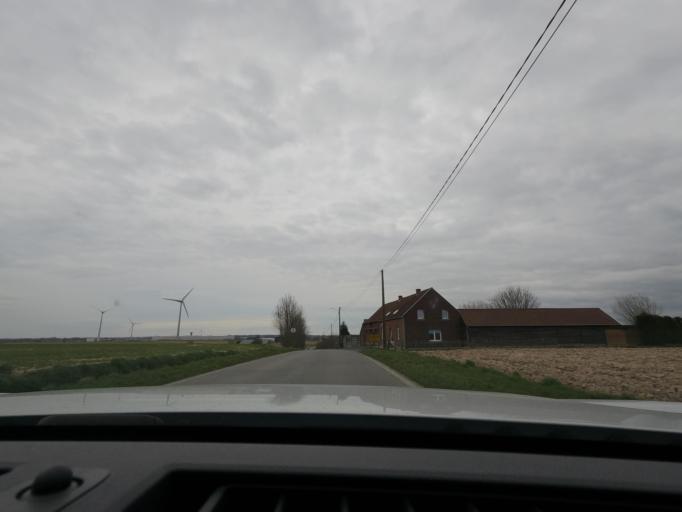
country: BE
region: Wallonia
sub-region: Province du Hainaut
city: Brugelette
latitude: 50.6419
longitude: 3.8660
